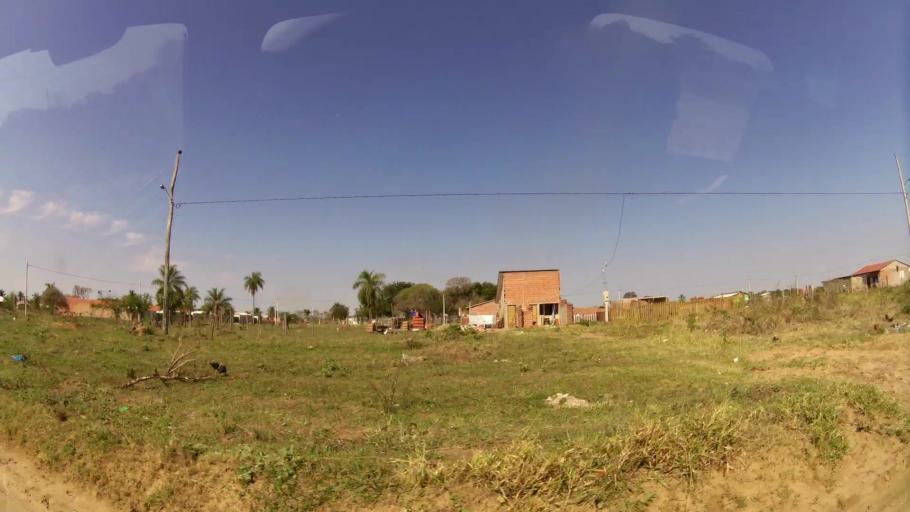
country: BO
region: Santa Cruz
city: Cotoca
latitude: -17.7167
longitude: -63.0655
